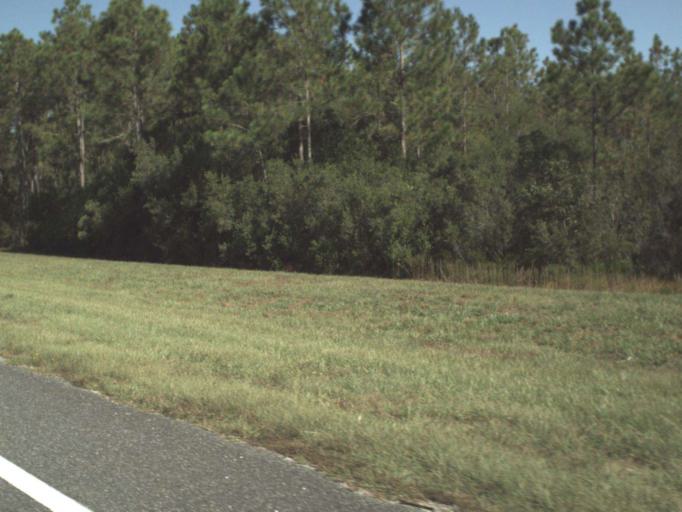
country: US
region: Florida
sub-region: Walton County
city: Seaside
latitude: 30.3222
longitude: -86.0474
